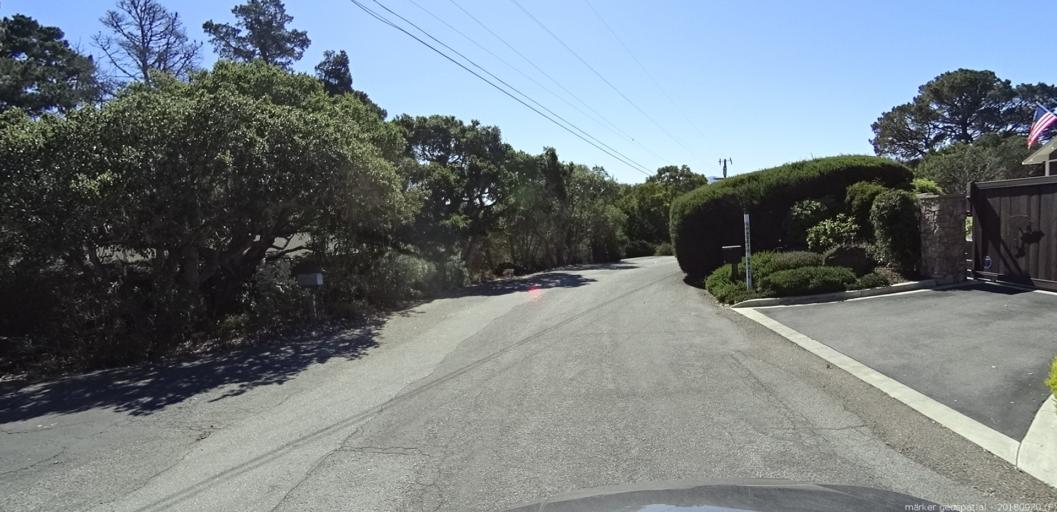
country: US
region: California
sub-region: Monterey County
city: Carmel-by-the-Sea
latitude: 36.5558
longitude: -121.9061
